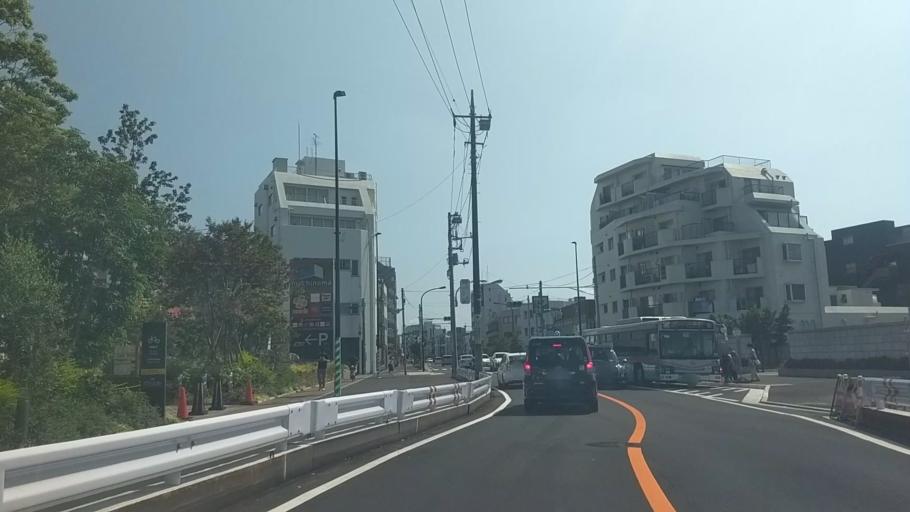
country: JP
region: Kanagawa
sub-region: Kawasaki-shi
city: Kawasaki
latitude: 35.5748
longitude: 139.7258
